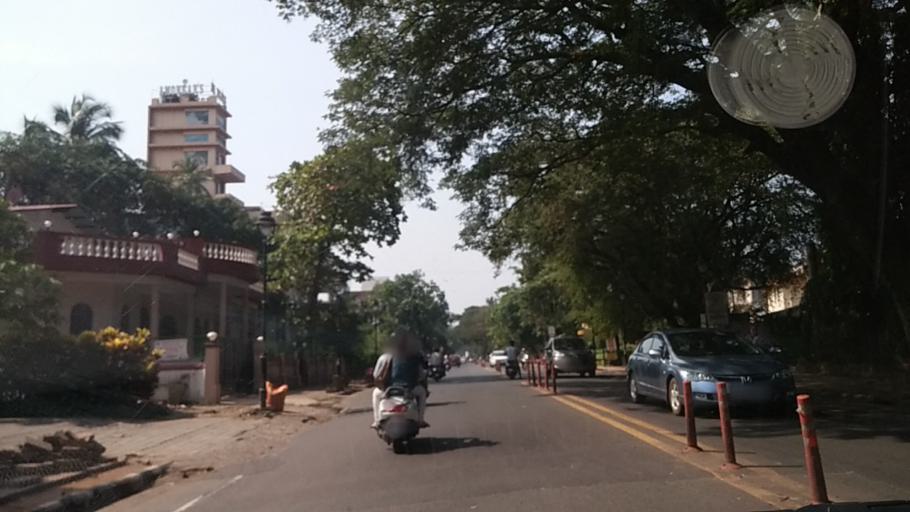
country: IN
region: Goa
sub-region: North Goa
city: Panaji
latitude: 15.4864
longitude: 73.8119
